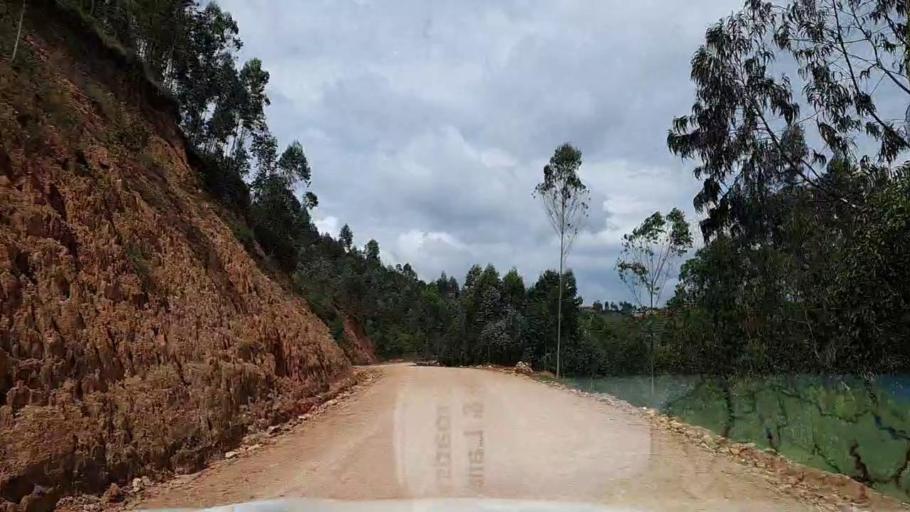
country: RW
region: Southern Province
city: Nzega
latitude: -2.3382
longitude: 29.4398
